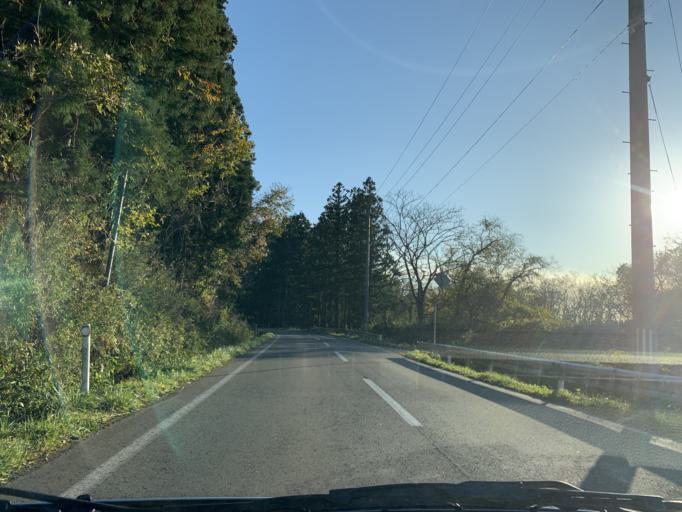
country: JP
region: Iwate
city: Mizusawa
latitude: 39.1212
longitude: 141.1857
